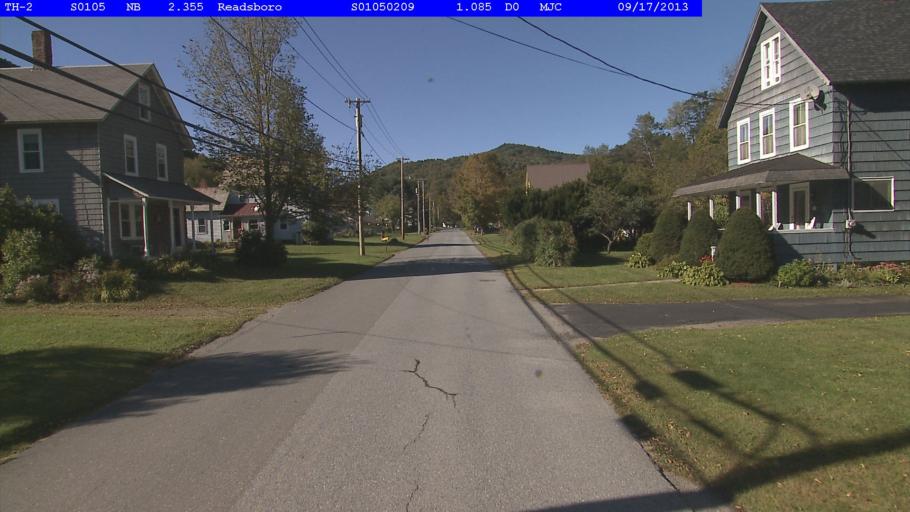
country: US
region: Massachusetts
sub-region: Franklin County
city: Charlemont
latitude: 42.7653
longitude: -72.9453
